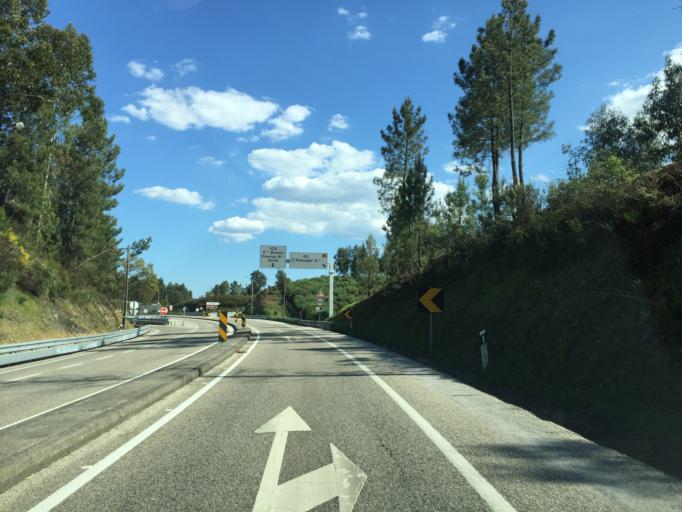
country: PT
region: Leiria
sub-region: Pedrogao Grande
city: Pedrogao Grande
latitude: 39.9119
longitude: -8.1535
